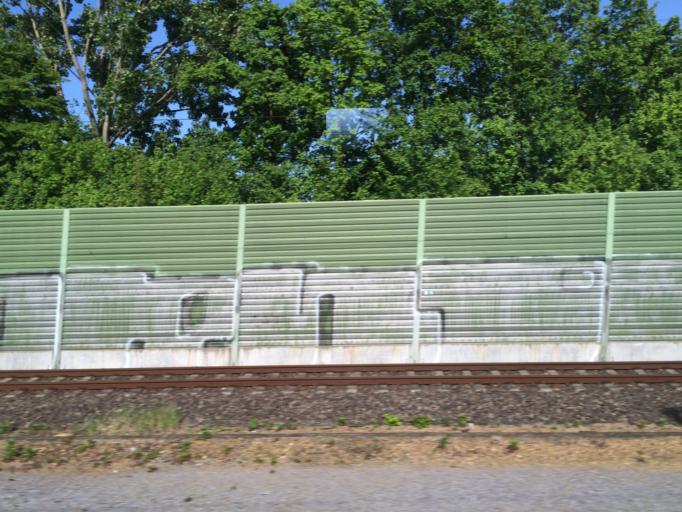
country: DE
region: North Rhine-Westphalia
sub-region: Regierungsbezirk Koln
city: Porz am Rhein
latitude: 50.8933
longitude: 7.0584
